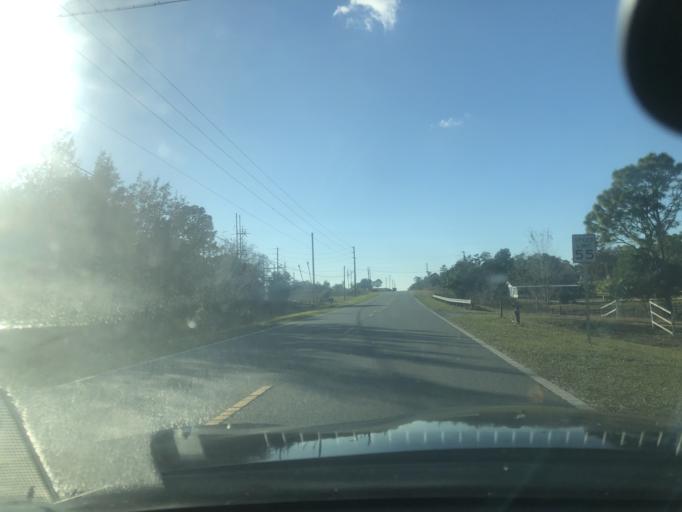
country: US
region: Florida
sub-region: Citrus County
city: Sugarmill Woods
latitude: 28.7640
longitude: -82.5148
